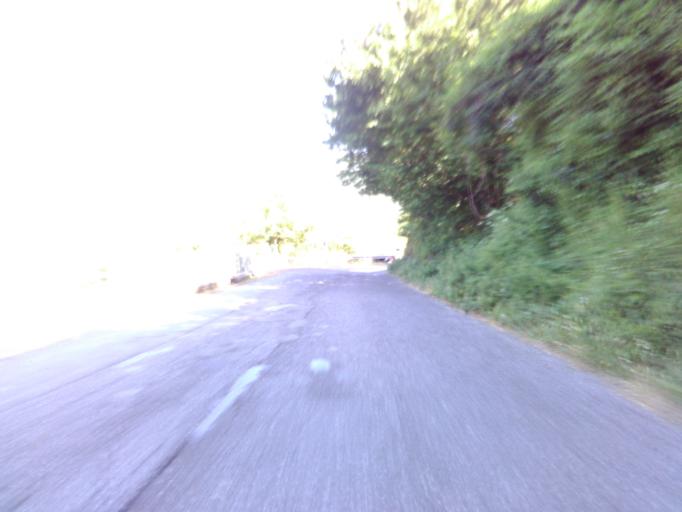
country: IT
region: Tuscany
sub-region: Provincia di Massa-Carrara
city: Licciana Nardi
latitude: 44.2993
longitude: 10.0722
